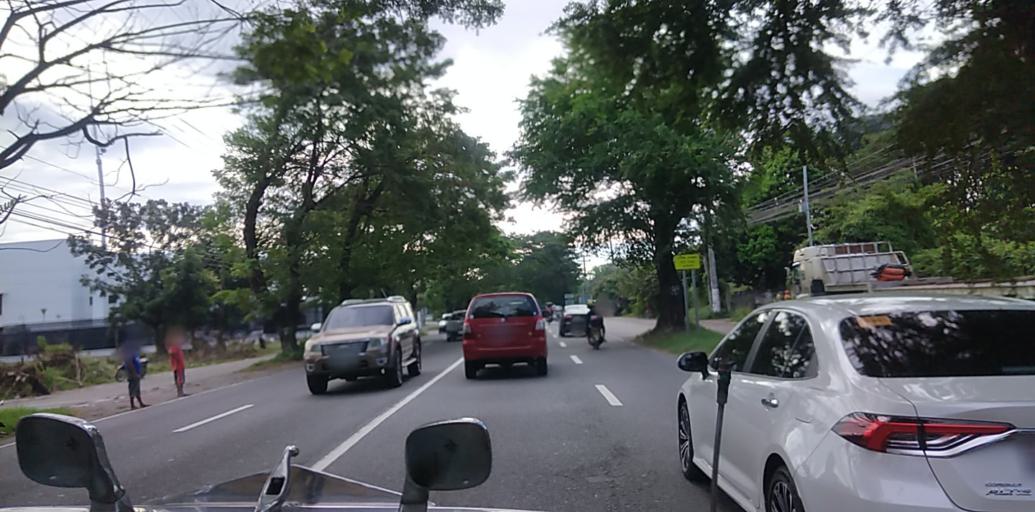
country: PH
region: Central Luzon
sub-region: Province of Pampanga
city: Bulaon
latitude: 15.0874
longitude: 120.6323
